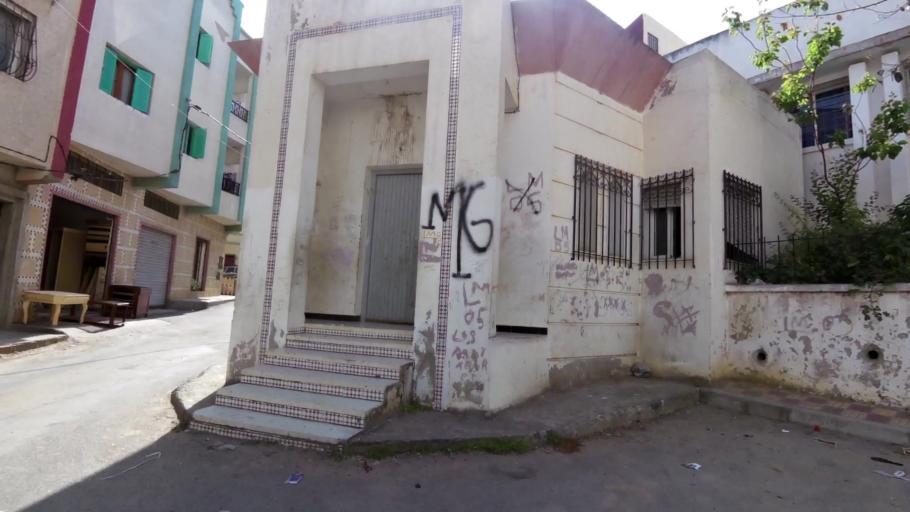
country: MA
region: Tanger-Tetouan
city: Tetouan
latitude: 35.5900
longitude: -5.3516
